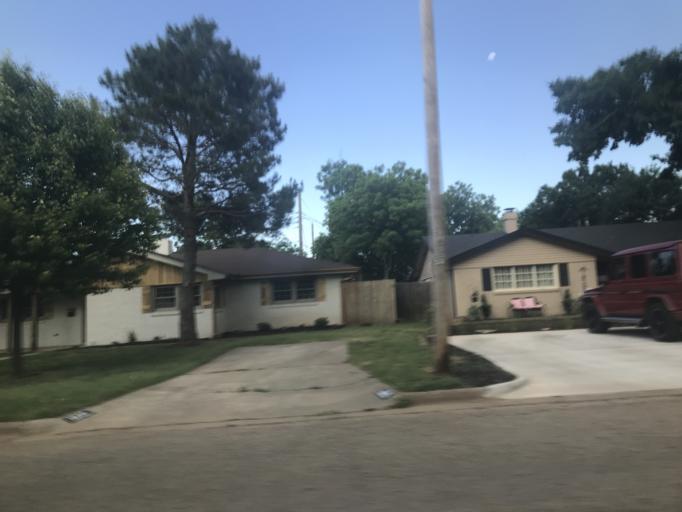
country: US
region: Texas
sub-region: Taylor County
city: Abilene
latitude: 32.4265
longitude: -99.7670
